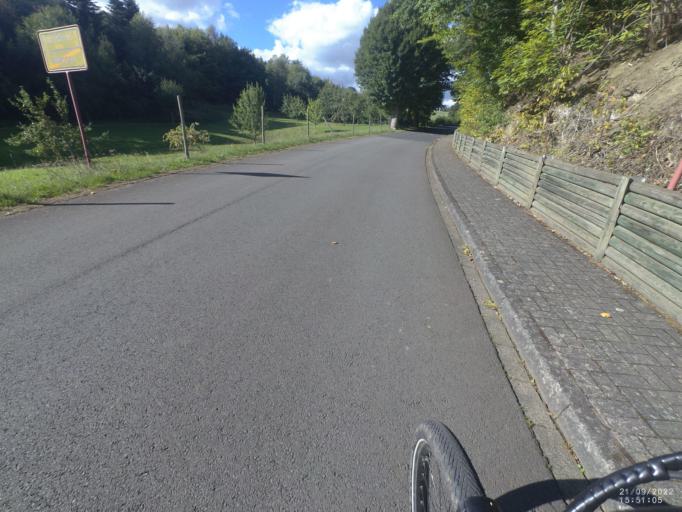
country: DE
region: Rheinland-Pfalz
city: Mehren
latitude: 50.1818
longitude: 6.8739
